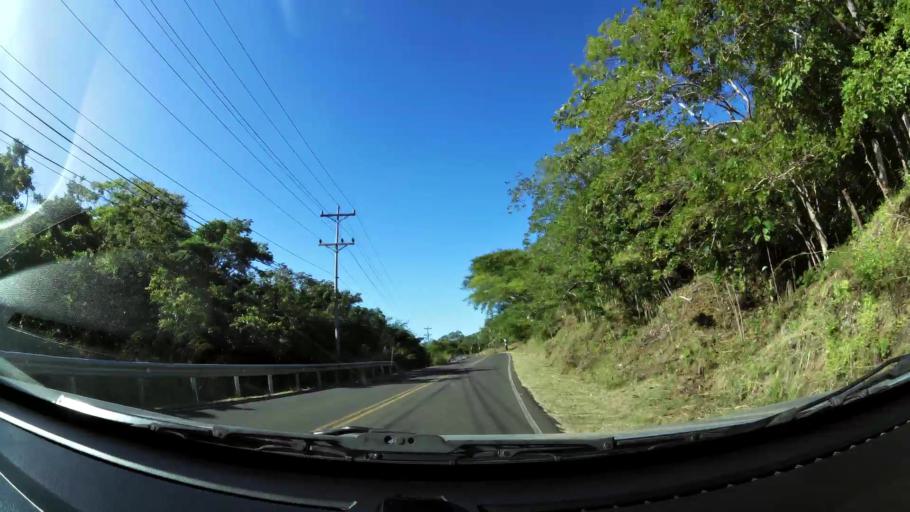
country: CR
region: Guanacaste
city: Belen
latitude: 10.3780
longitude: -85.6215
